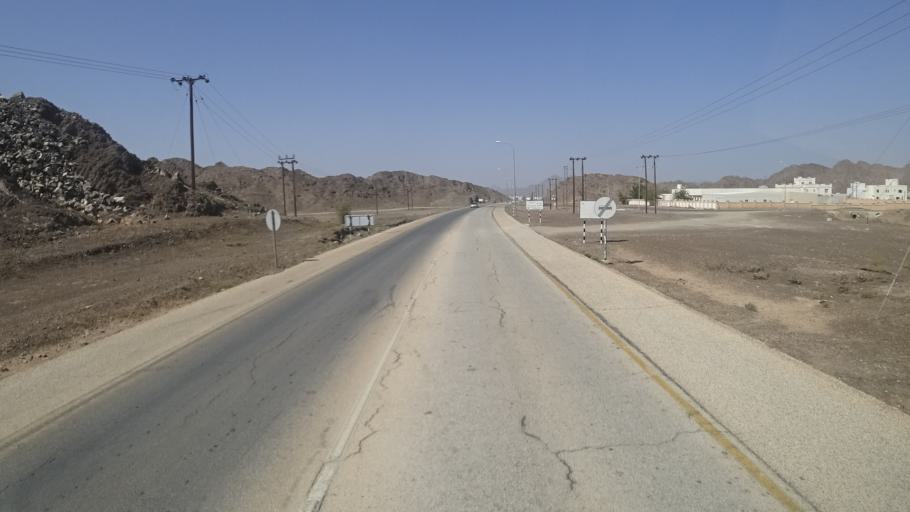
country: OM
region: Ash Sharqiyah
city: Ibra'
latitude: 22.6839
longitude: 58.5678
